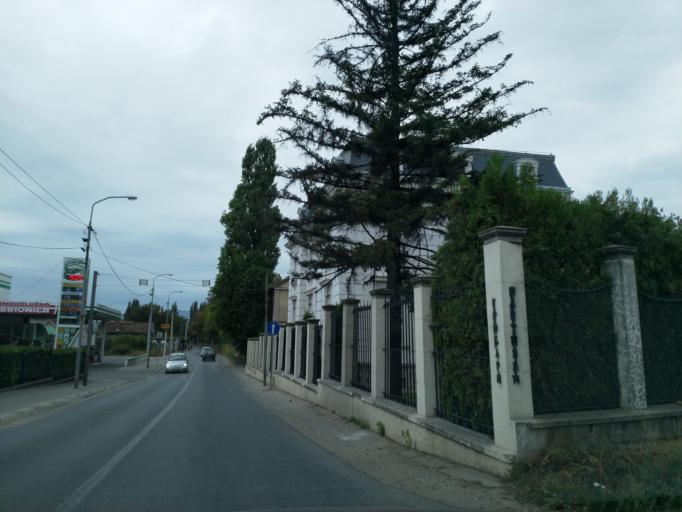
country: RS
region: Central Serbia
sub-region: Pomoravski Okrug
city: Paracin
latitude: 43.8580
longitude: 21.4039
